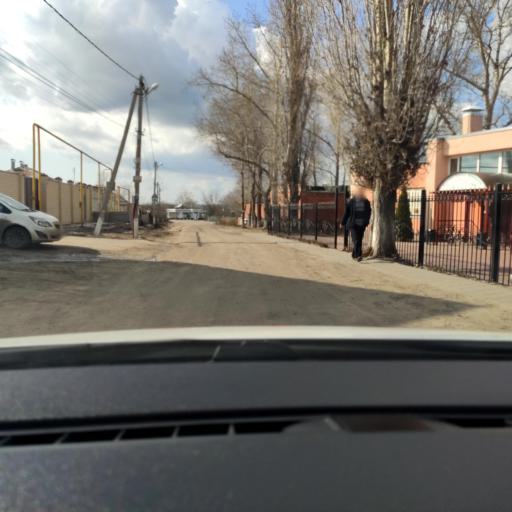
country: RU
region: Voronezj
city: Podgornoye
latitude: 51.7324
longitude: 39.1509
